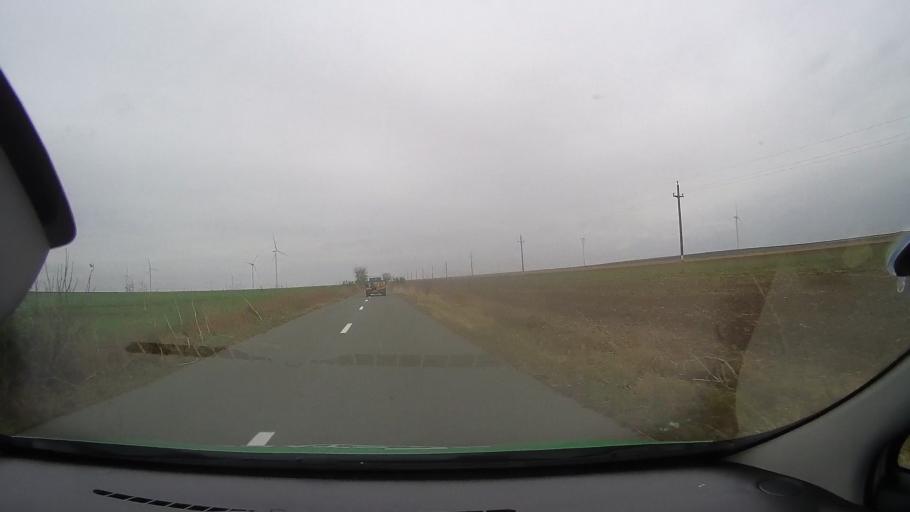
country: RO
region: Constanta
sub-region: Comuna Targusor
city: Targusor
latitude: 44.4728
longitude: 28.3847
